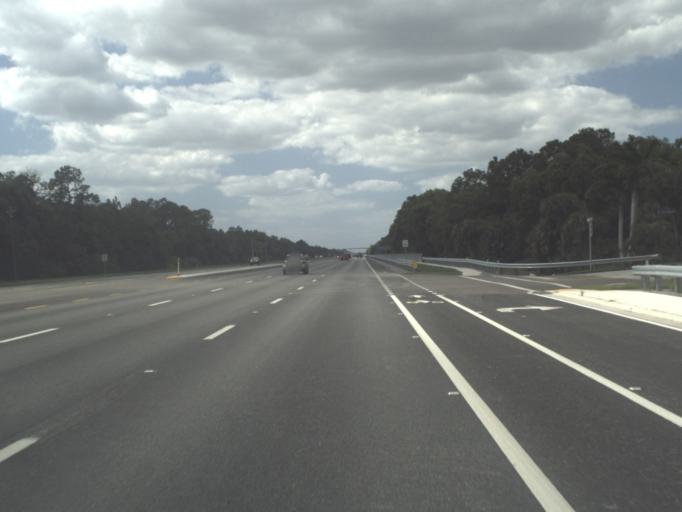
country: US
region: Florida
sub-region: Collier County
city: Lely Resort
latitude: 26.0451
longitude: -81.6707
